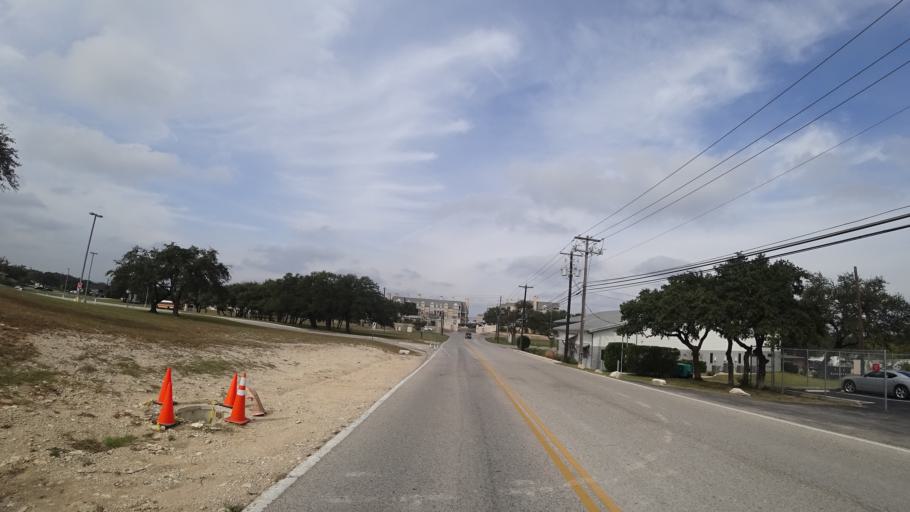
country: US
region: Texas
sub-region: Travis County
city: Hudson Bend
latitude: 30.3921
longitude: -97.9344
